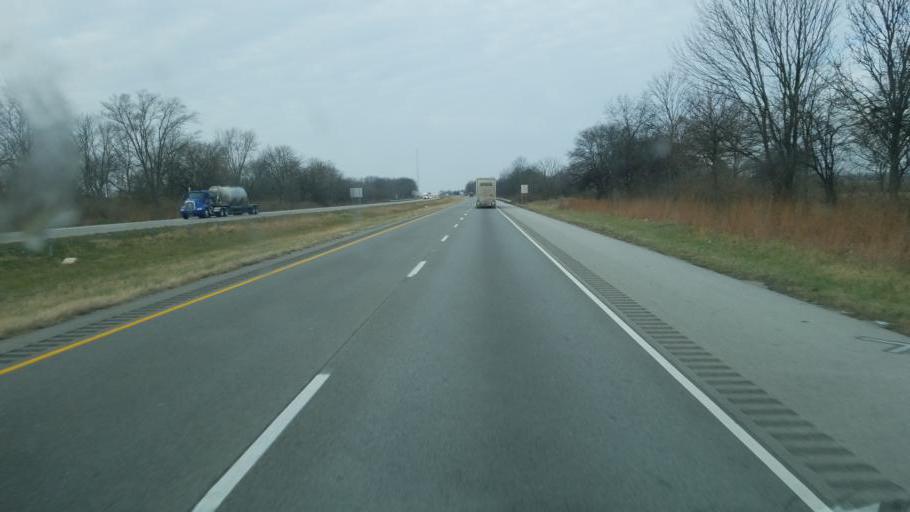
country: US
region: Indiana
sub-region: Morgan County
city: Monrovia
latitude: 39.6080
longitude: -86.4980
